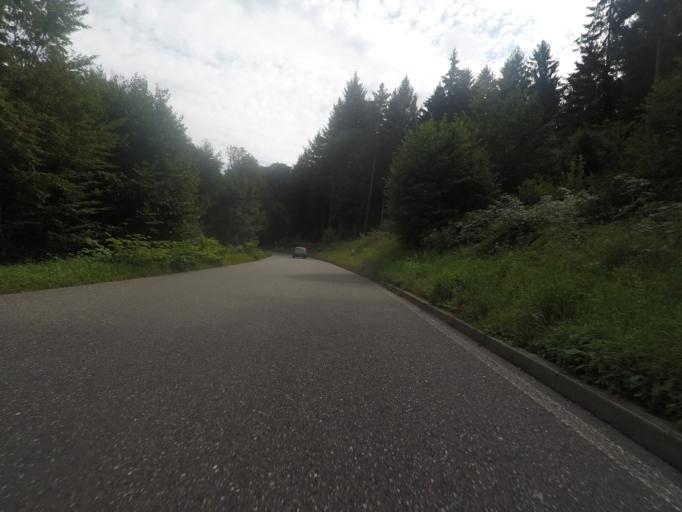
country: DE
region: Baden-Wuerttemberg
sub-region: Karlsruhe Region
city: Bad Herrenalb
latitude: 48.8563
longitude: 8.4065
